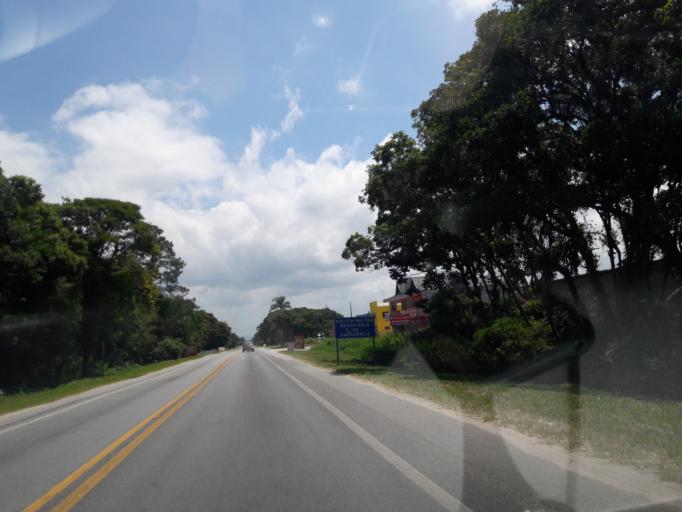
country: BR
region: Parana
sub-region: Pontal Do Parana
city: Pontal do Parana
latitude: -25.6906
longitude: -48.4859
